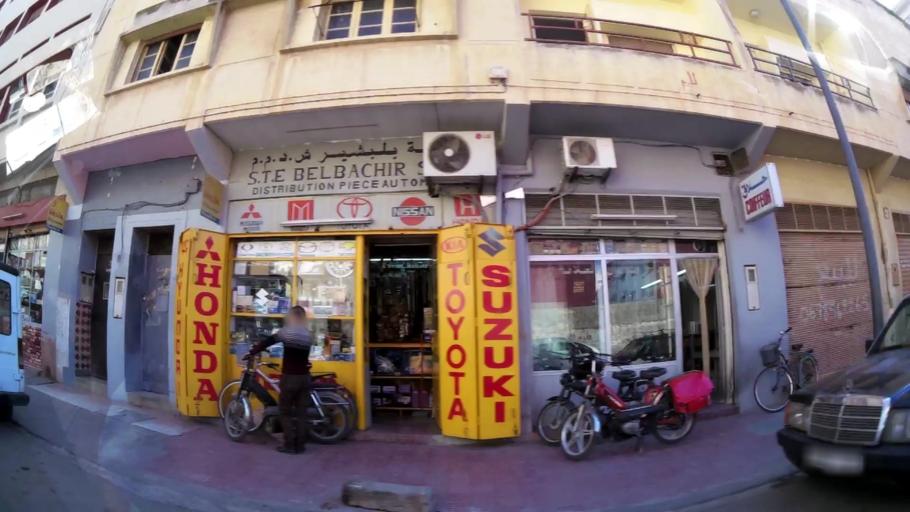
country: MA
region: Oriental
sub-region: Oujda-Angad
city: Oujda
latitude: 34.6857
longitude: -1.9157
